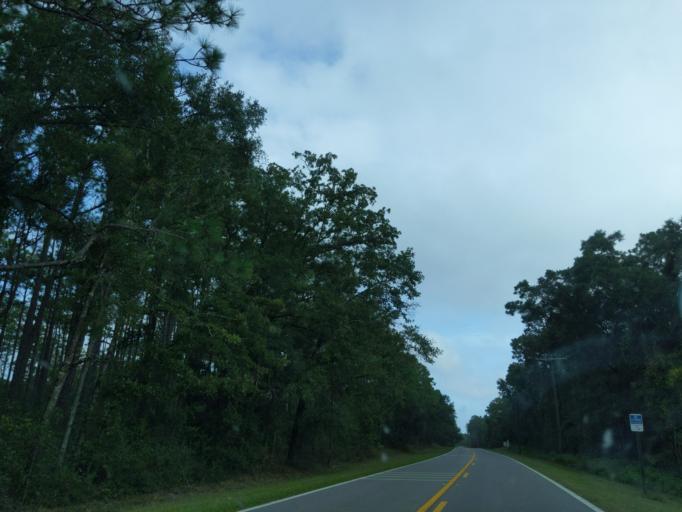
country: US
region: Florida
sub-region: Wakulla County
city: Crawfordville
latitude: 30.1198
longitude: -84.3145
